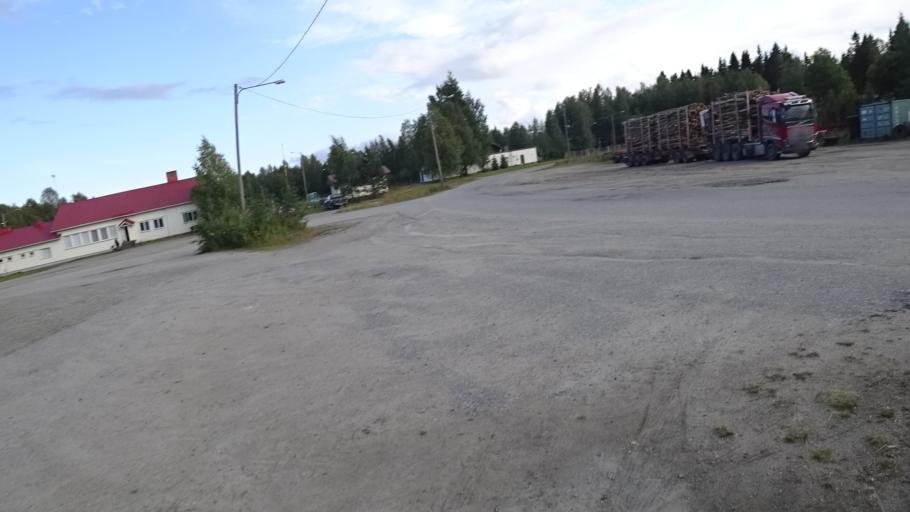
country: FI
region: North Karelia
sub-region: Joensuu
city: Ilomantsi
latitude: 62.6719
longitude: 30.9473
